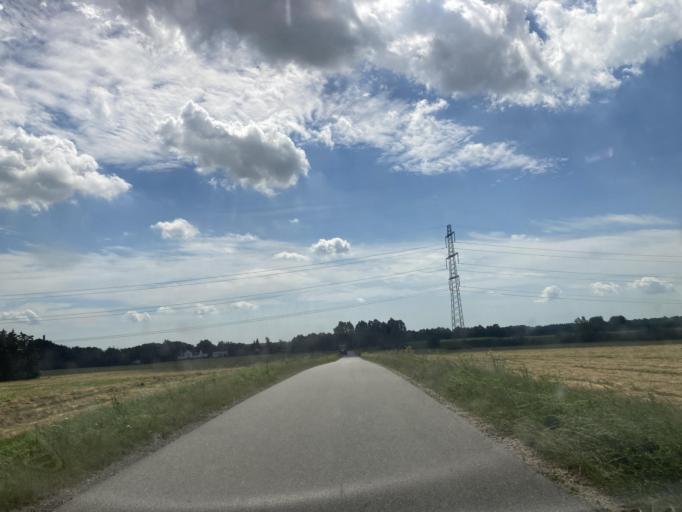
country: DK
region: Zealand
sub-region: Koge Kommune
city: Borup
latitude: 55.4547
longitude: 11.9488
